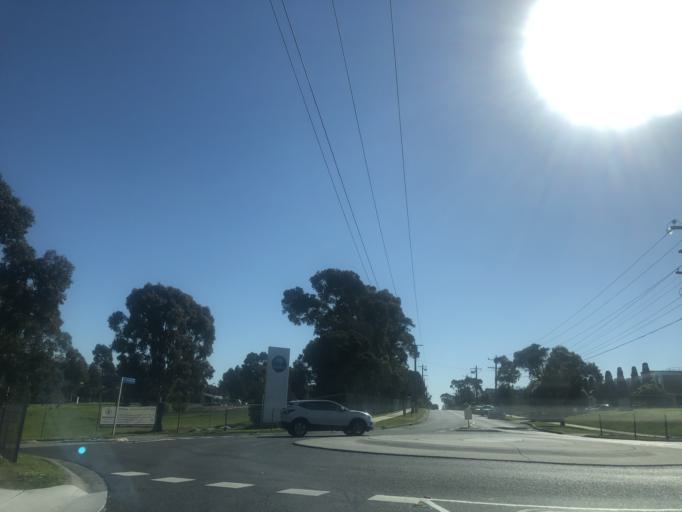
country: AU
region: Victoria
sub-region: Monash
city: Notting Hill
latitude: -37.9062
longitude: 145.1376
